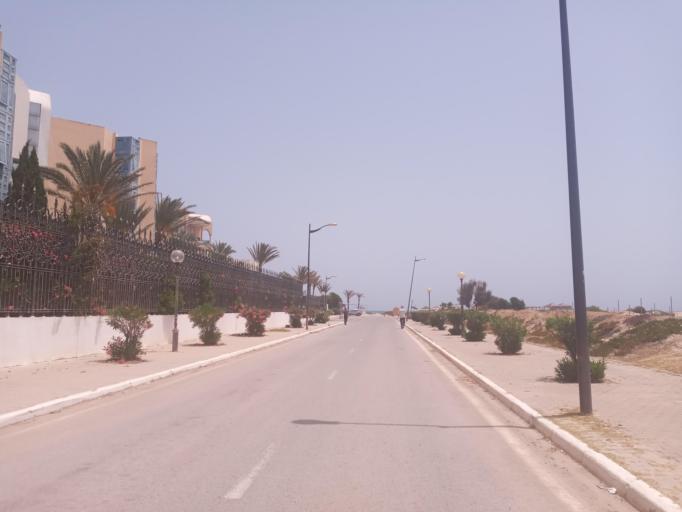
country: TN
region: Nabul
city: Al Hammamat
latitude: 36.3545
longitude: 10.5278
